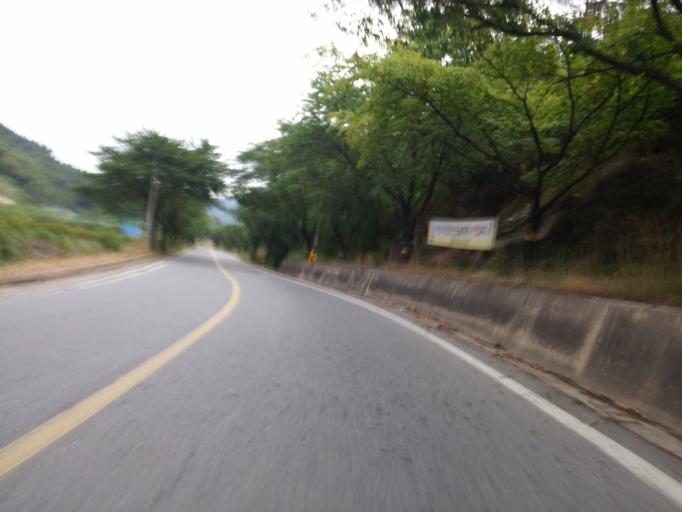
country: KR
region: Chungcheongnam-do
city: Kinzan
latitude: 36.1717
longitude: 127.5322
